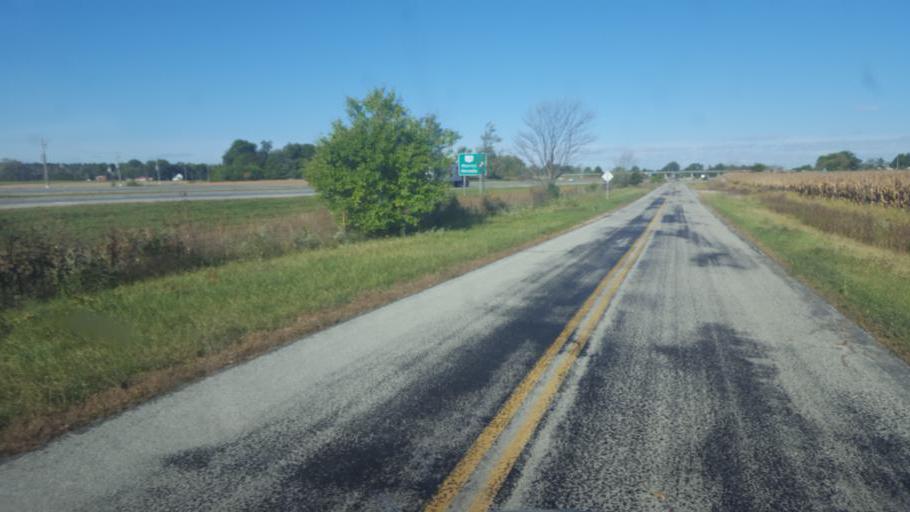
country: US
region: Ohio
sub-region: Marion County
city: Marion
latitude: 40.6886
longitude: -83.1440
